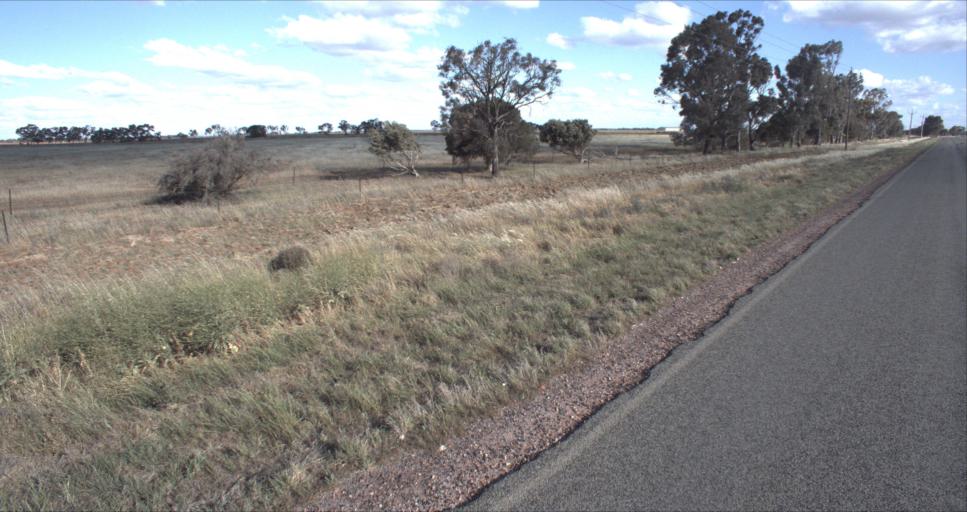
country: AU
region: New South Wales
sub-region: Leeton
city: Leeton
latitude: -34.5340
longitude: 146.2809
